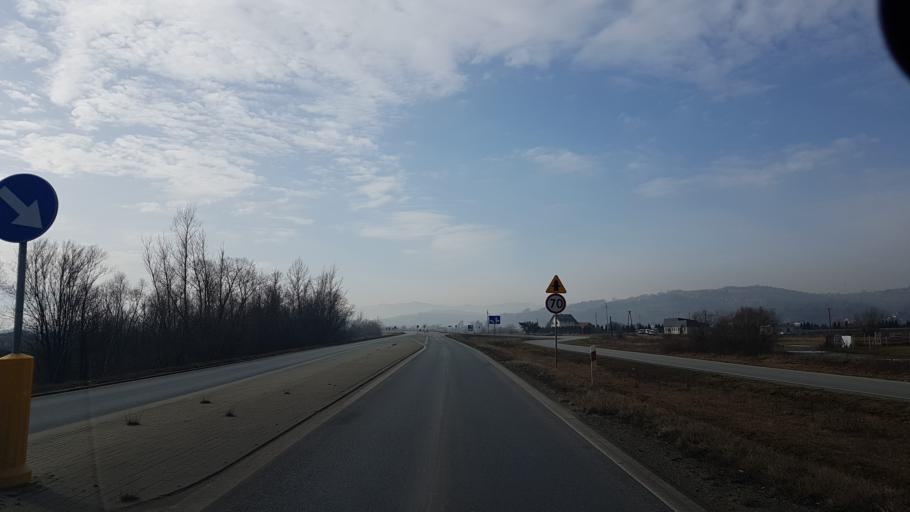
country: PL
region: Lesser Poland Voivodeship
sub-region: Powiat nowosadecki
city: Podegrodzie
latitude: 49.5733
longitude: 20.6045
